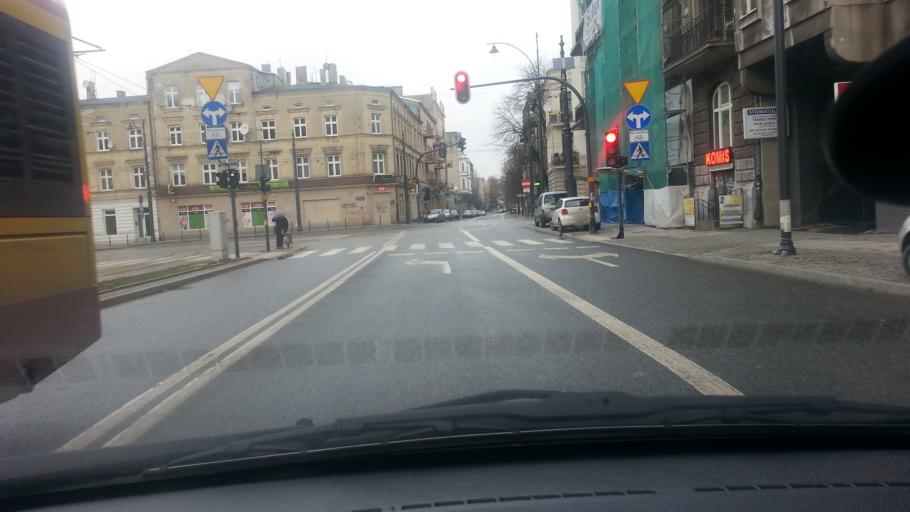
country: PL
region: Lodz Voivodeship
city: Lodz
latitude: 51.7711
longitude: 19.4670
